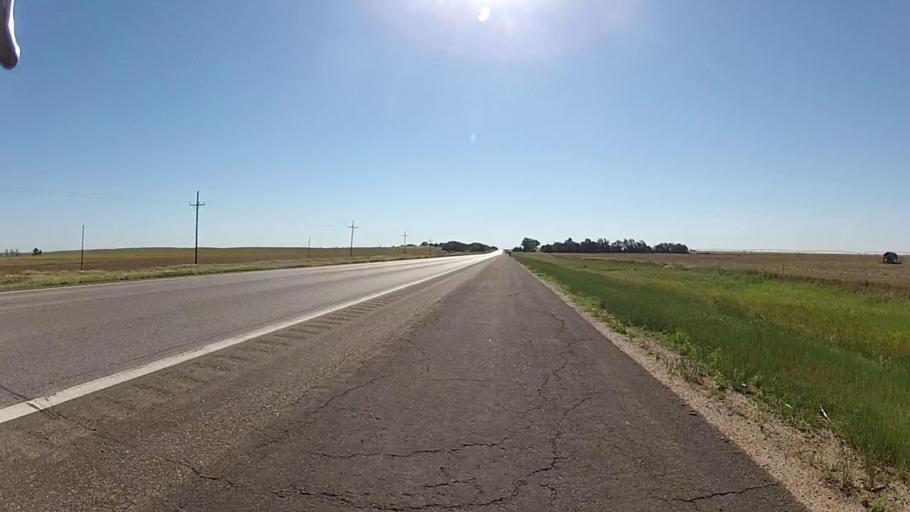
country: US
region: Kansas
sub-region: Kiowa County
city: Greensburg
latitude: 37.5866
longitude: -99.5900
